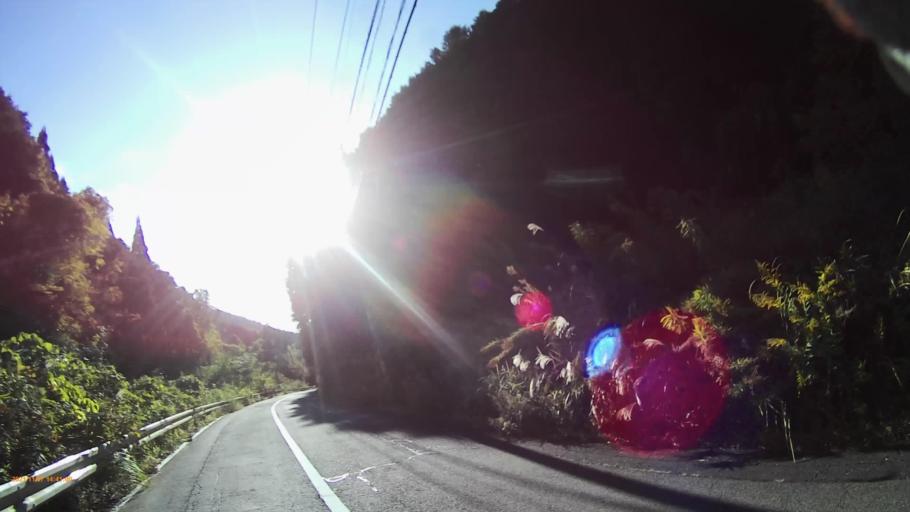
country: JP
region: Gifu
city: Mitake
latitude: 35.4341
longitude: 137.1689
